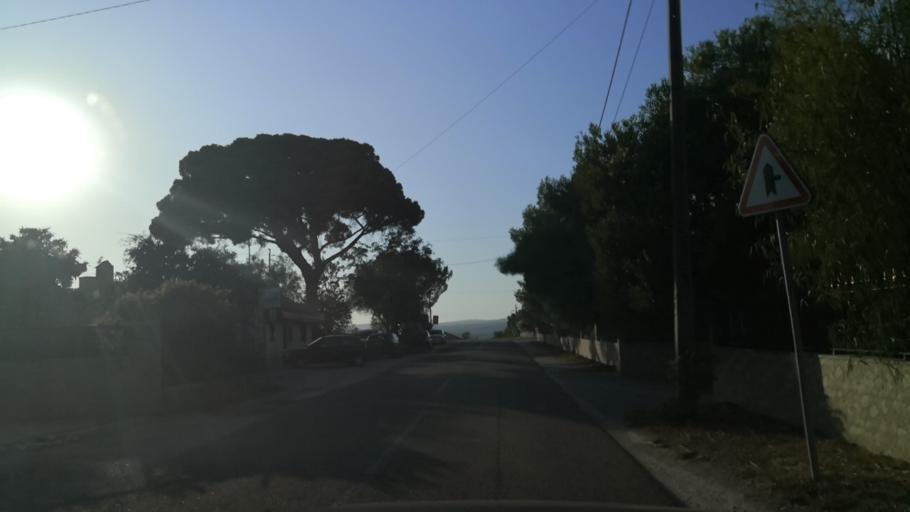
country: PT
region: Santarem
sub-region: Alcanena
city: Alcanena
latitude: 39.4583
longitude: -8.6355
